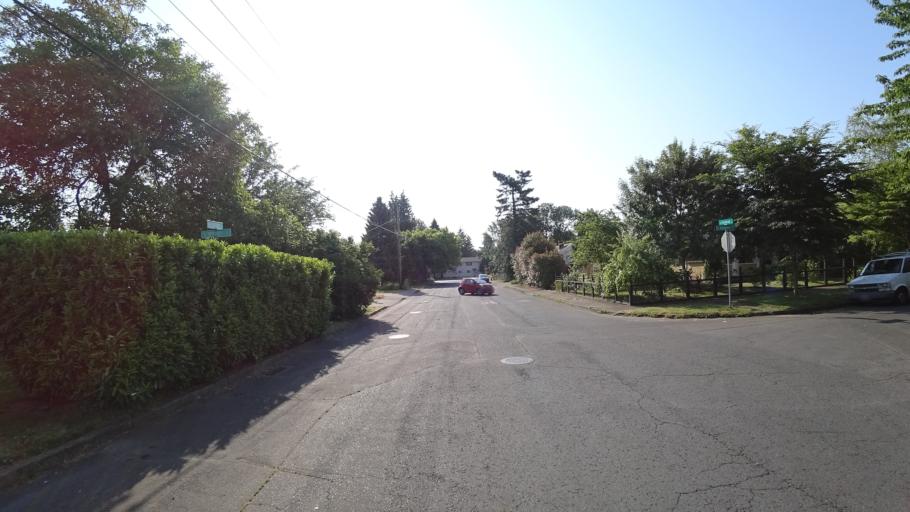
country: US
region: Oregon
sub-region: Washington County
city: West Haven
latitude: 45.5880
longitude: -122.7369
